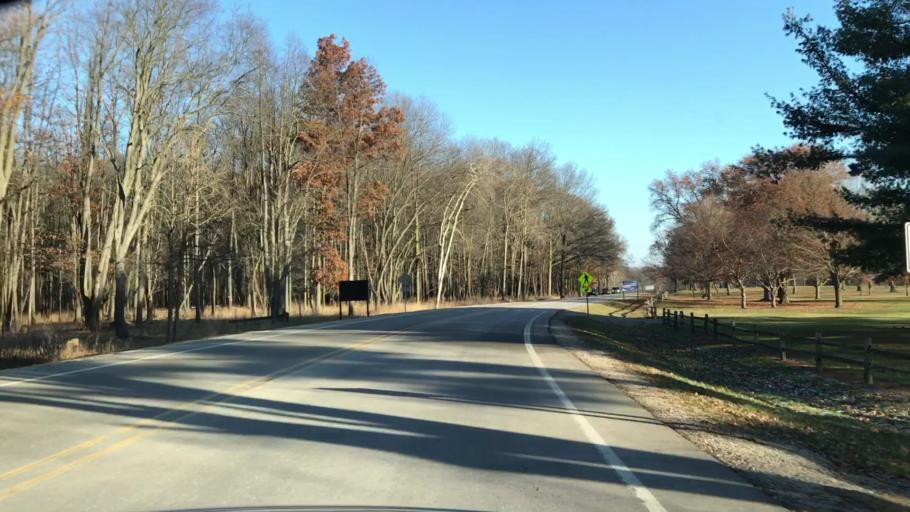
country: US
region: Michigan
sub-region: Oakland County
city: South Lyon
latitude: 42.5233
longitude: -83.6852
